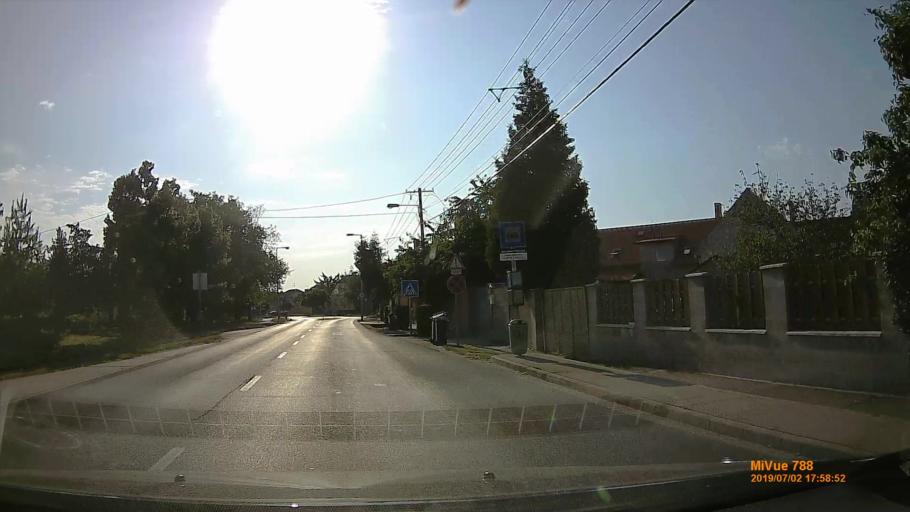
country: HU
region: Gyor-Moson-Sopron
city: Mosonmagyarovar
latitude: 47.8517
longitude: 17.2734
